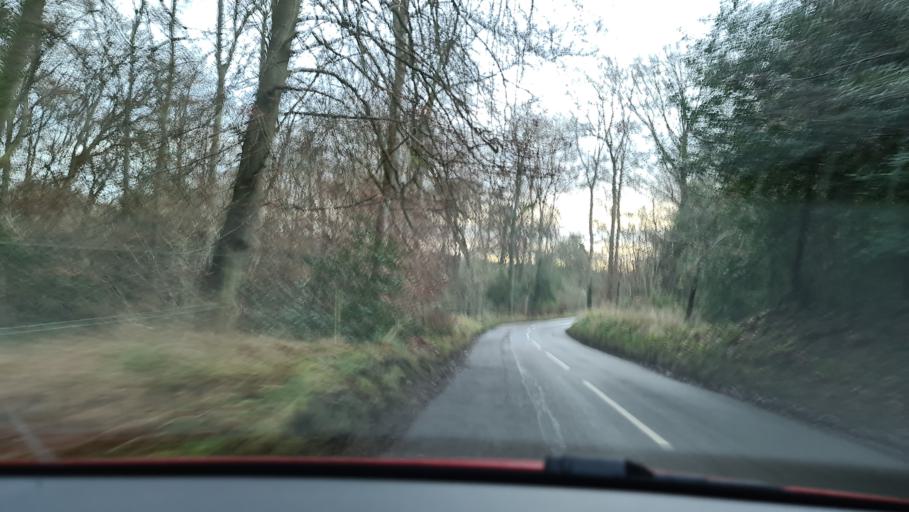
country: GB
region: England
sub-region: Buckinghamshire
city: Great Missenden
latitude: 51.7124
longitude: -0.7617
